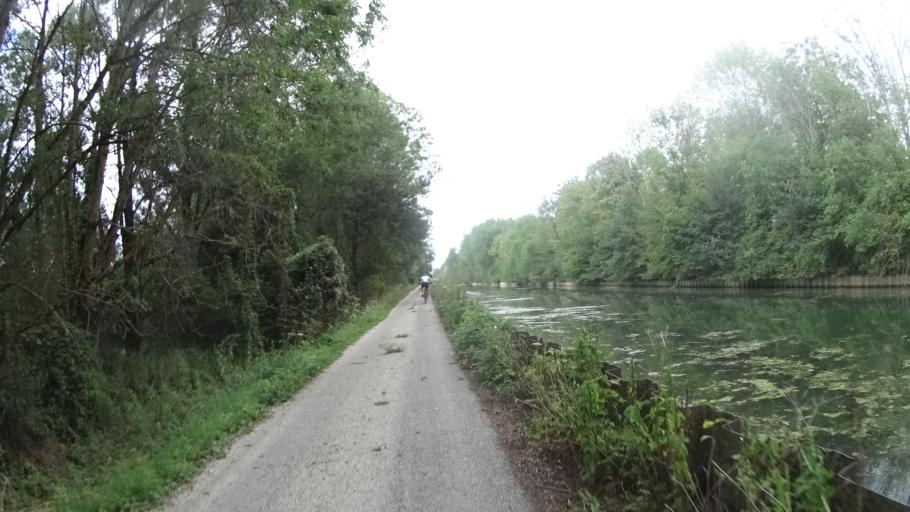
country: FR
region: Picardie
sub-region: Departement de l'Aisne
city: Itancourt
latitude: 49.7565
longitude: 3.3799
